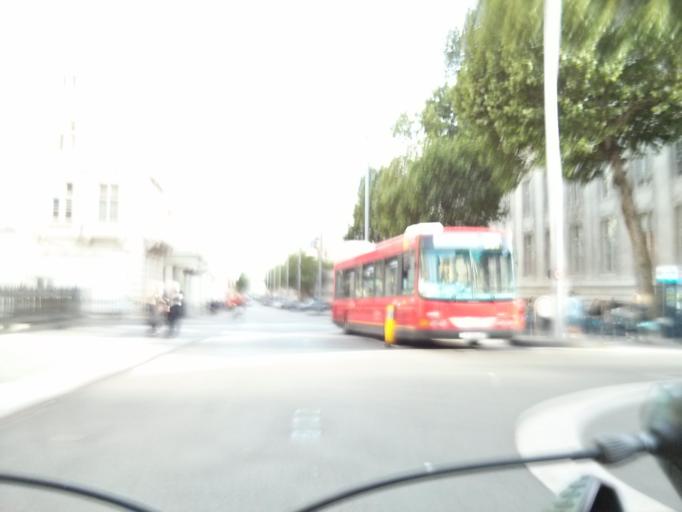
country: GB
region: England
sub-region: Greater London
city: Chelsea
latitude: 51.5001
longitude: -0.1745
